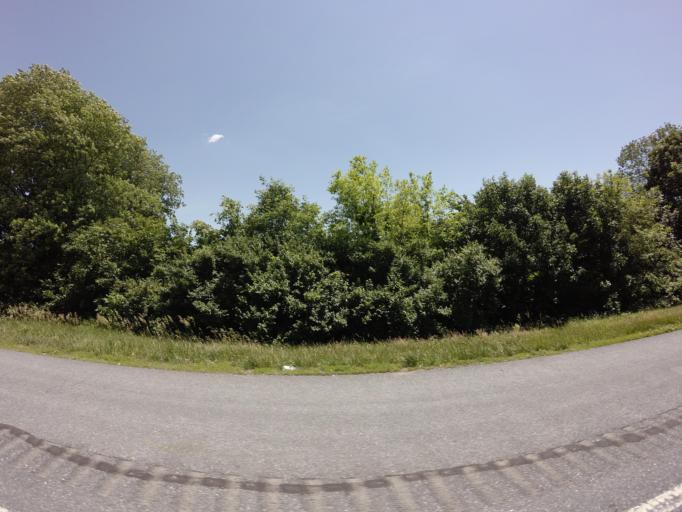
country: US
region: Maryland
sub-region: Frederick County
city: Brunswick
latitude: 39.3344
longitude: -77.6490
